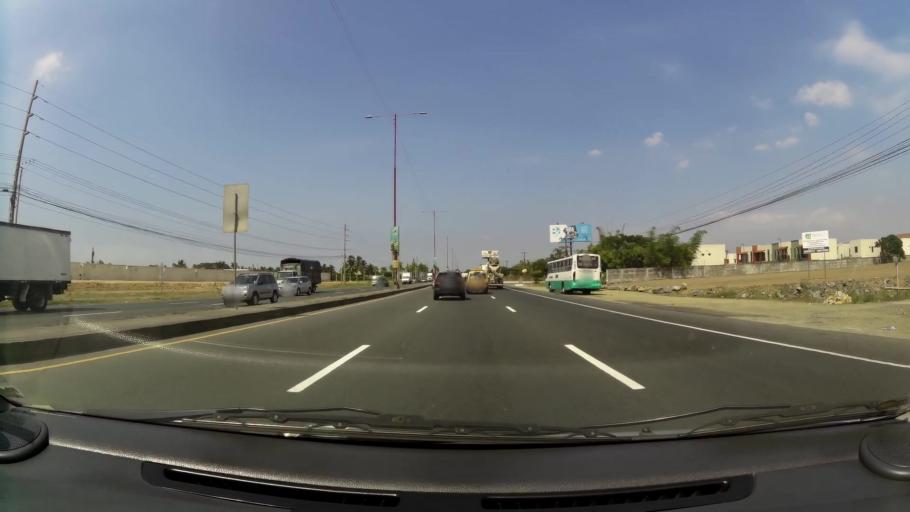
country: EC
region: Guayas
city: El Triunfo
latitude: -2.0503
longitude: -79.9031
